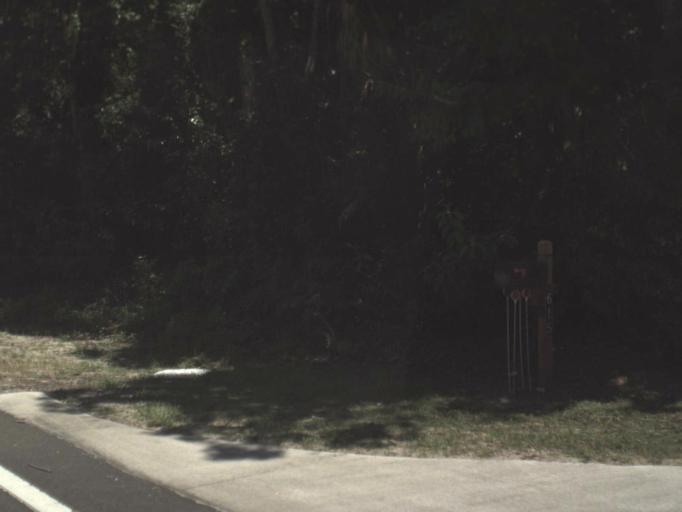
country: US
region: Florida
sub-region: Clay County
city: Keystone Heights
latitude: 29.7165
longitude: -82.0102
